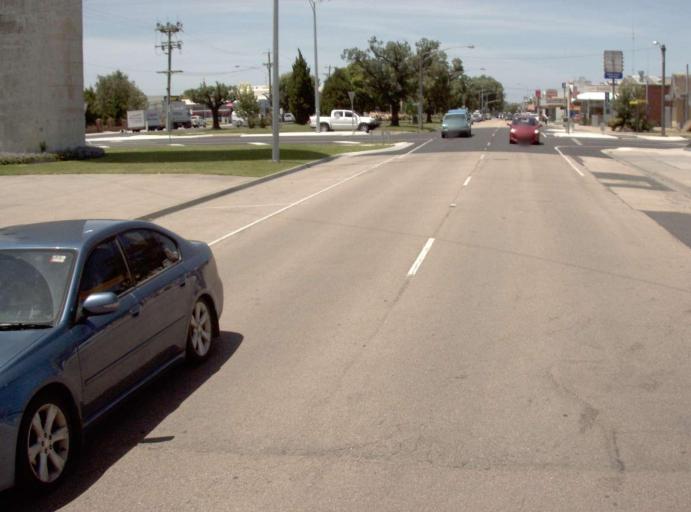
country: AU
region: Victoria
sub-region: East Gippsland
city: Bairnsdale
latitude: -37.8273
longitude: 147.6262
